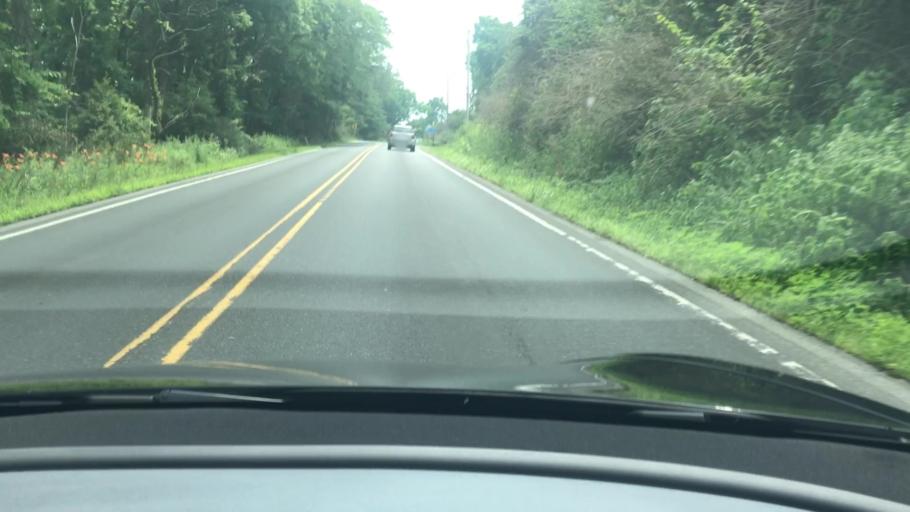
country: US
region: Pennsylvania
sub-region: Centre County
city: Park Forest Village
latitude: 40.8275
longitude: -77.9667
